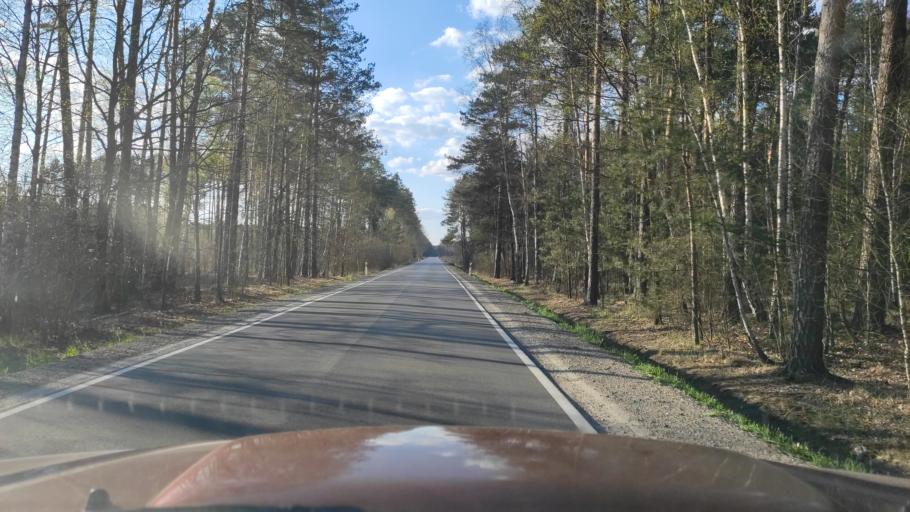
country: PL
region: Masovian Voivodeship
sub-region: Powiat zwolenski
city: Zwolen
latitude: 51.3934
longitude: 21.5460
